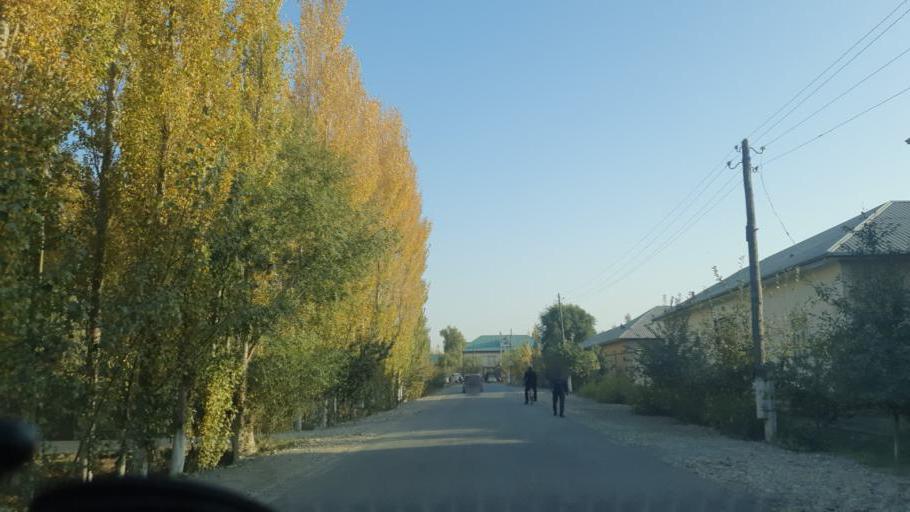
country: UZ
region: Fergana
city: Beshariq
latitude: 40.4632
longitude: 70.5434
